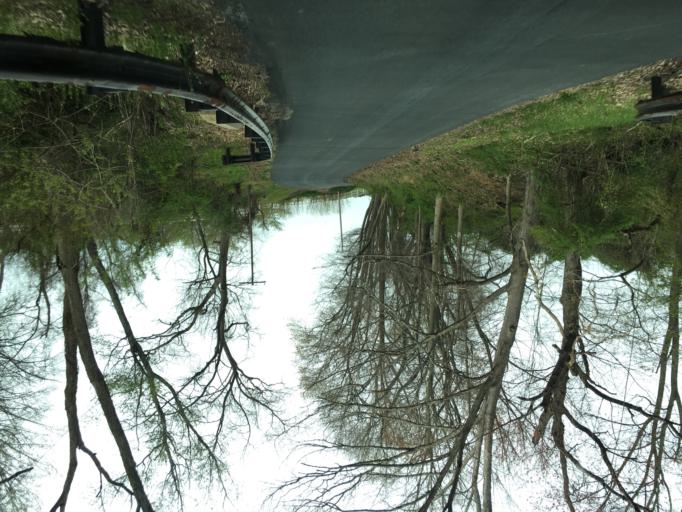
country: US
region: Maryland
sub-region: Baltimore County
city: Hunt Valley
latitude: 39.5690
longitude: -76.6269
